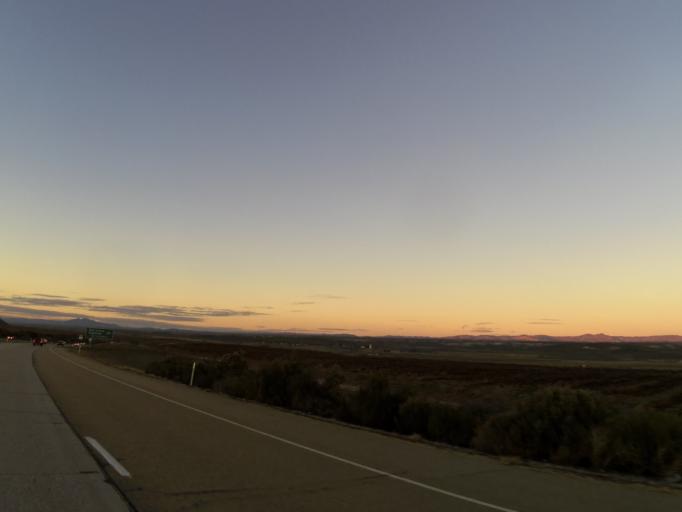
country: US
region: California
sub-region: Monterey County
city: King City
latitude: 36.0963
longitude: -121.0239
